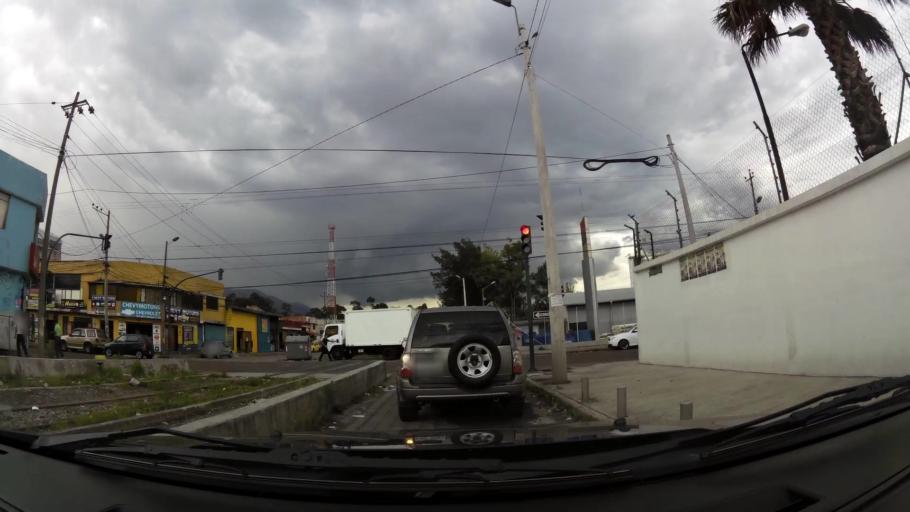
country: EC
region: Pichincha
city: Quito
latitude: -0.2763
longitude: -78.5334
